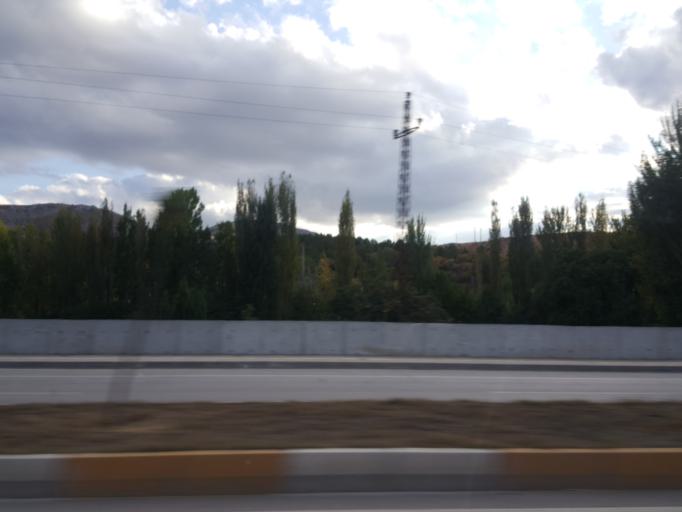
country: TR
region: Tokat
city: Tokat
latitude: 40.3367
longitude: 36.5020
